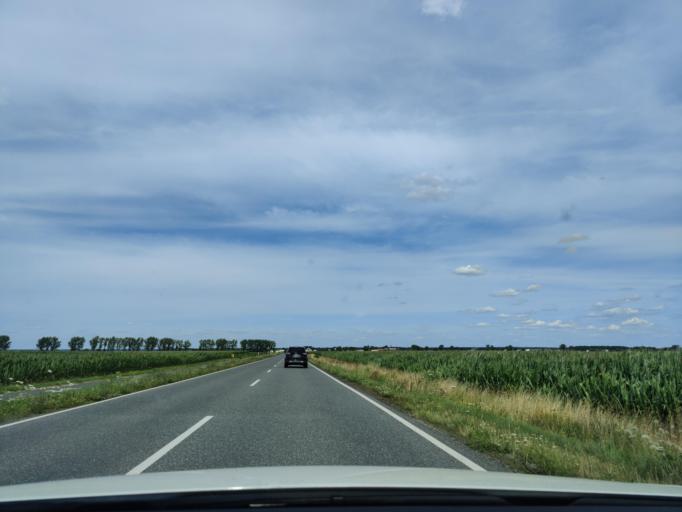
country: PL
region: Opole Voivodeship
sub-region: Powiat prudnicki
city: Biala
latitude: 50.4083
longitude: 17.7065
